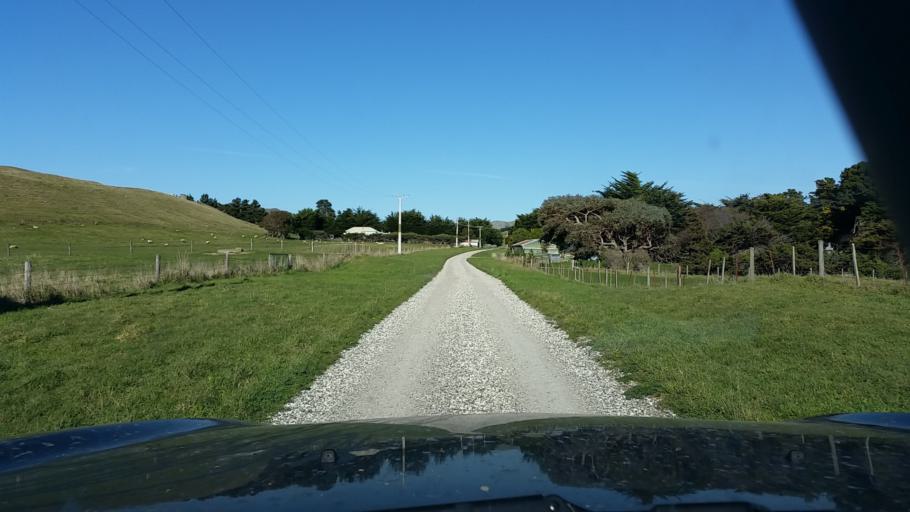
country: NZ
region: Marlborough
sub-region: Marlborough District
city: Blenheim
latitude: -41.7389
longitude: 174.1664
